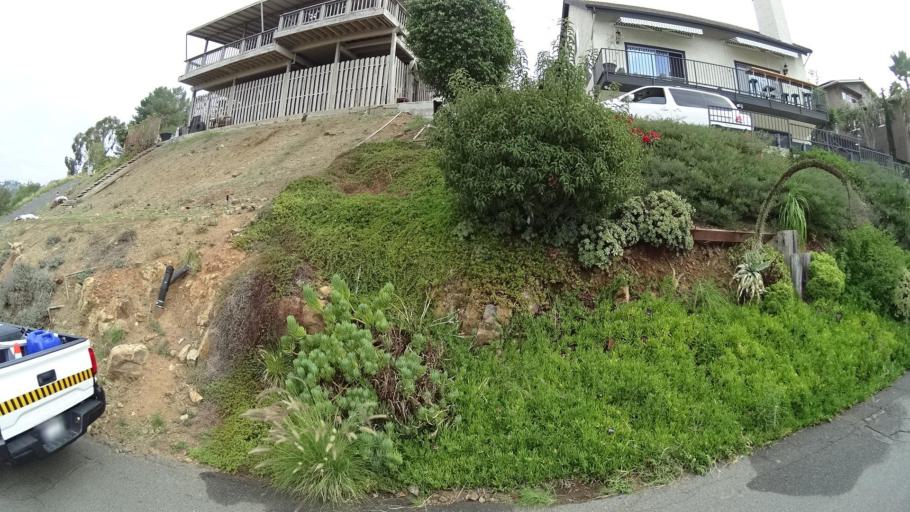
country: US
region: California
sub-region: San Diego County
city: Spring Valley
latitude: 32.7424
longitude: -117.0114
